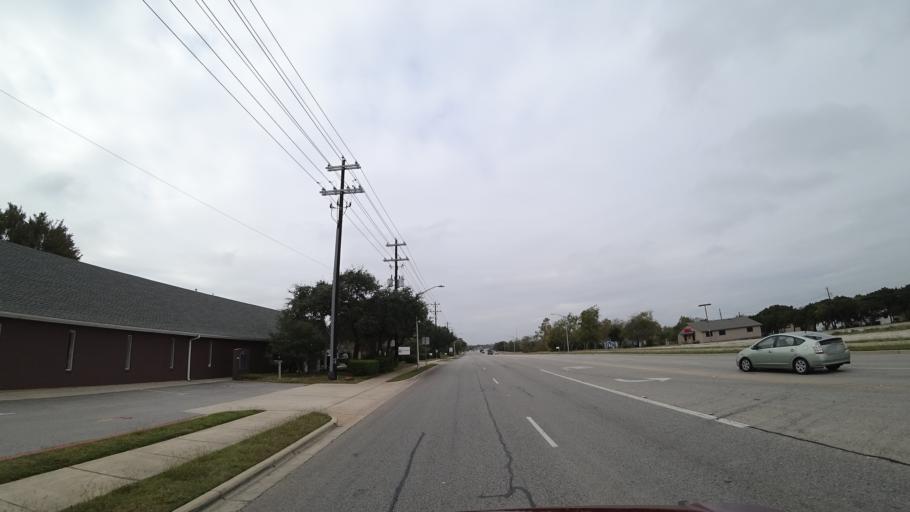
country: US
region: Texas
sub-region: Williamson County
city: Cedar Park
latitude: 30.5325
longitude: -97.8363
